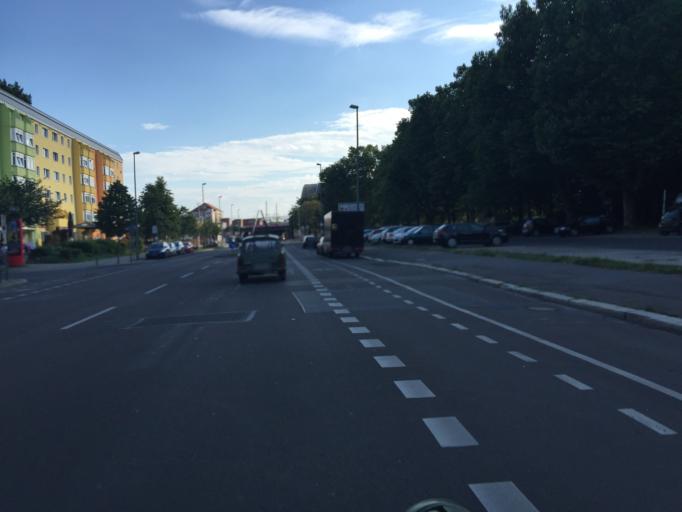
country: DE
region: Berlin
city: Friedrichshain Bezirk
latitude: 52.5123
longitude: 13.4385
